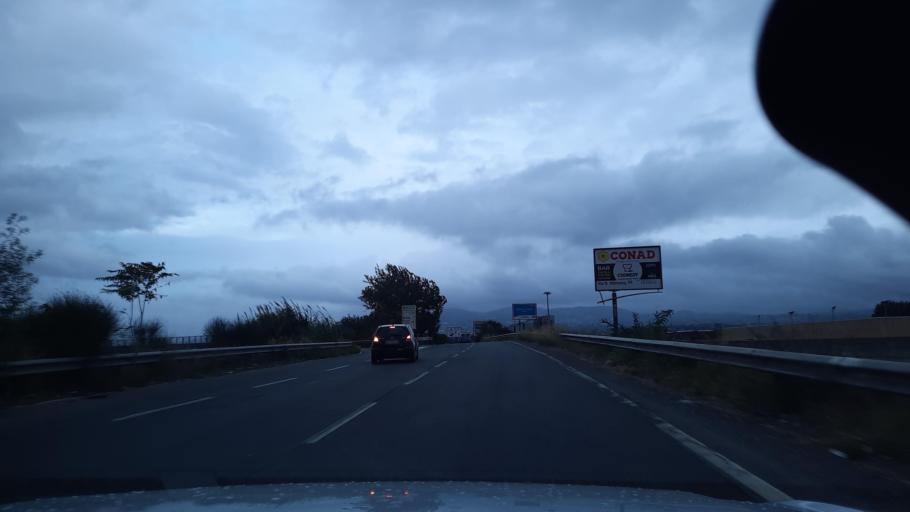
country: IT
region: Latium
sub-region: Citta metropolitana di Roma Capitale
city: Ciampino
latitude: 41.8482
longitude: 12.6100
